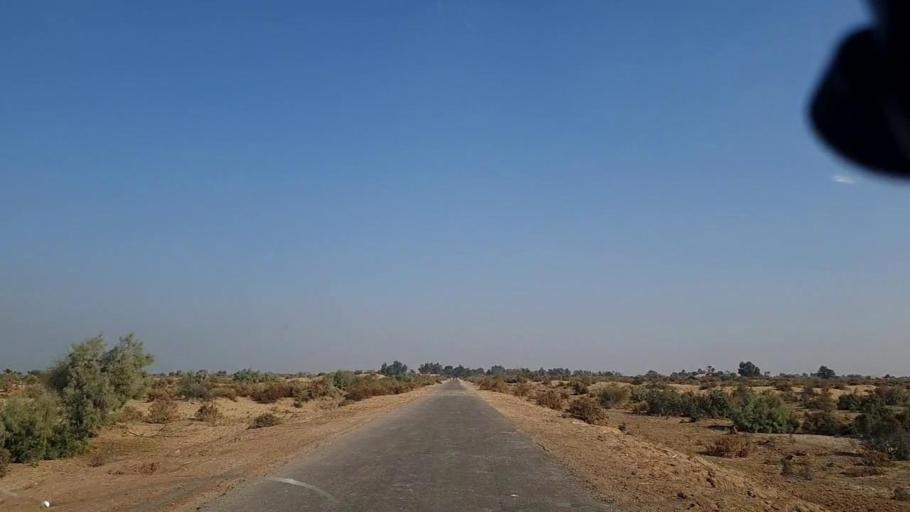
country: PK
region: Sindh
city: Khanpur
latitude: 27.6865
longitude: 69.4778
